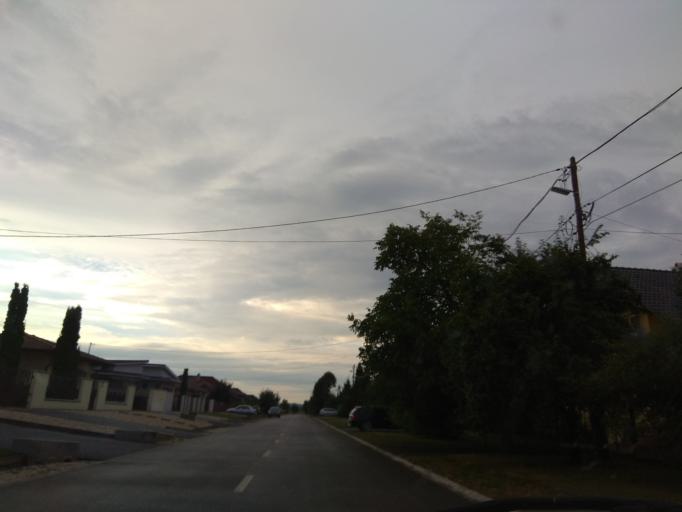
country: HU
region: Borsod-Abauj-Zemplen
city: Miskolc
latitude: 48.0733
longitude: 20.8206
